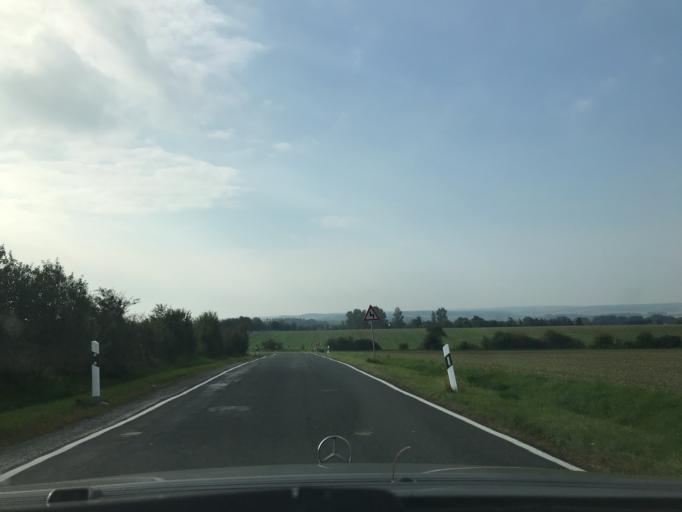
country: DE
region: Thuringia
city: Helmsdorf
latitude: 51.2636
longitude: 10.3982
